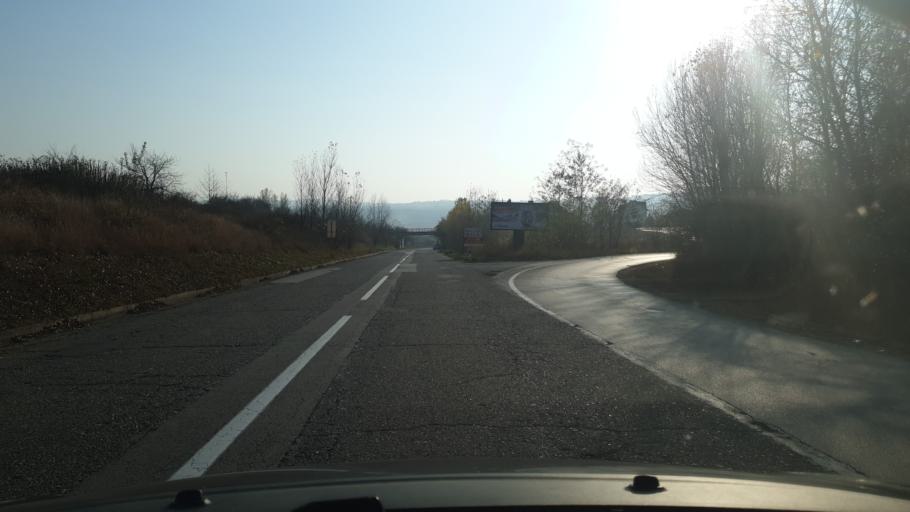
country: RS
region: Central Serbia
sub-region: Borski Okrug
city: Negotin
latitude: 44.2397
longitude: 22.5153
